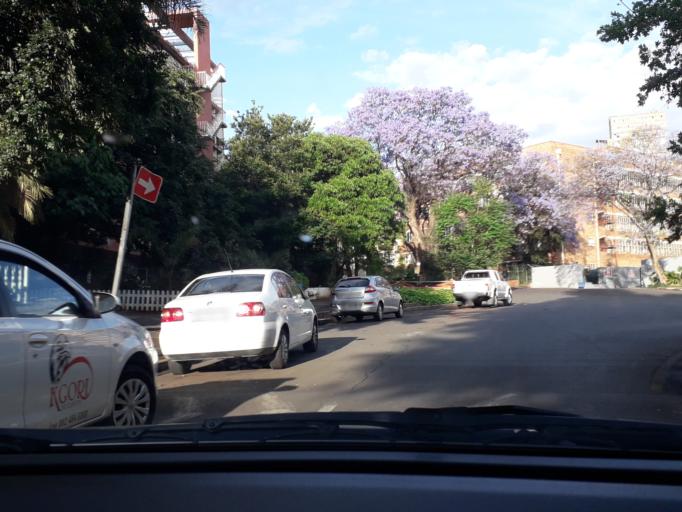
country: ZA
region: Gauteng
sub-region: City of Johannesburg Metropolitan Municipality
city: Johannesburg
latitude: -26.1837
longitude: 28.0456
